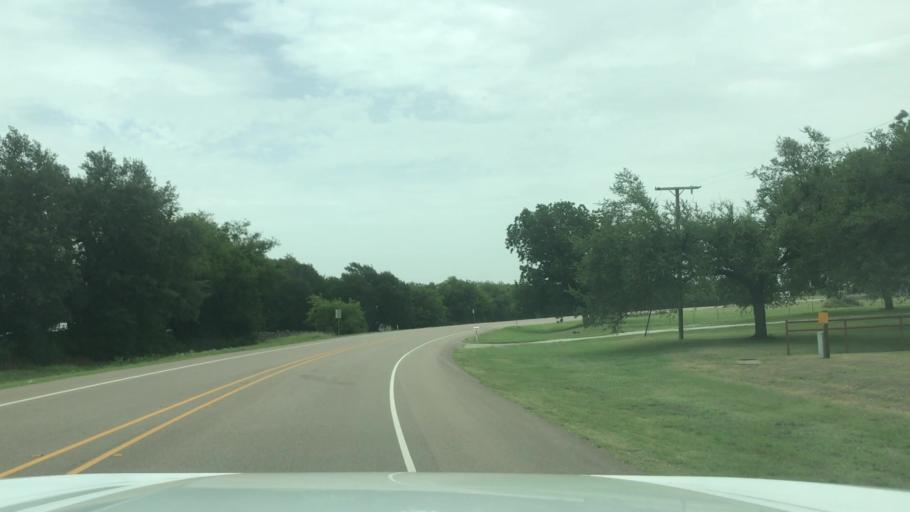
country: US
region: Texas
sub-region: Hamilton County
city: Hico
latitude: 31.9825
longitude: -97.8685
